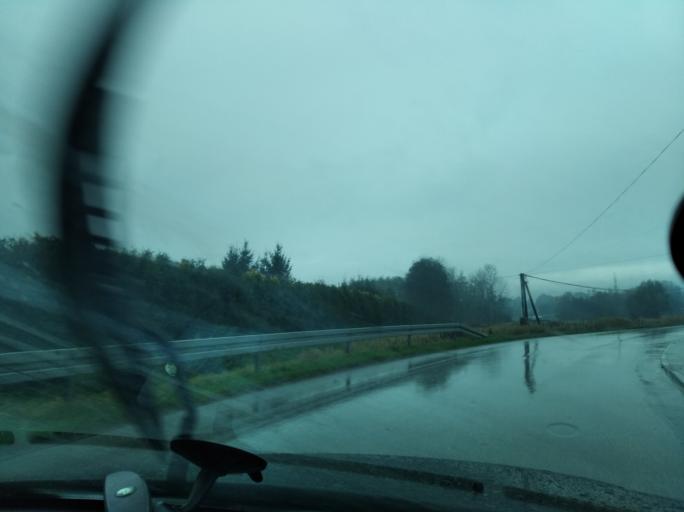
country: PL
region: Subcarpathian Voivodeship
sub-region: Powiat lancucki
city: Albigowa
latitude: 50.0359
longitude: 22.2086
